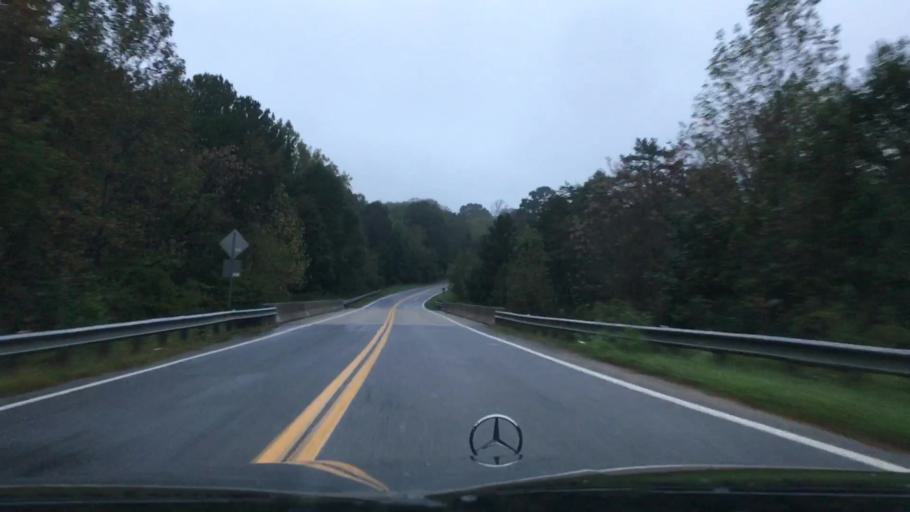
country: US
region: Virginia
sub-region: Campbell County
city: Timberlake
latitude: 37.2415
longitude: -79.2802
